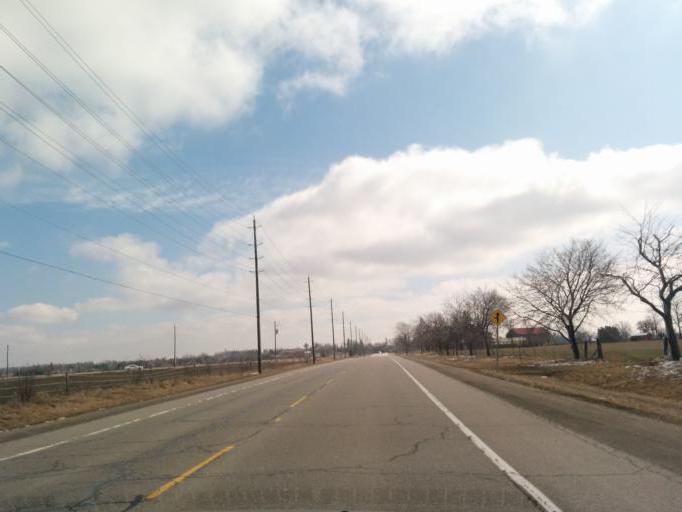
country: CA
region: Ontario
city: Waterloo
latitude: 43.5180
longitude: -80.4641
